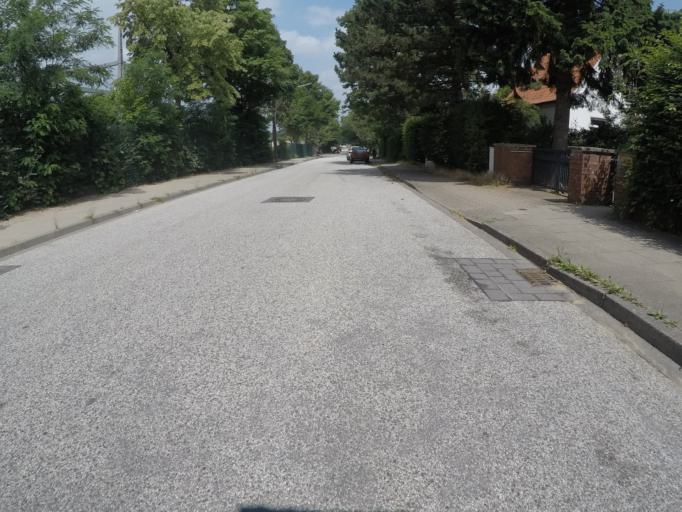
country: DE
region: Hamburg
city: Eidelstedt
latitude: 53.5817
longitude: 9.8726
